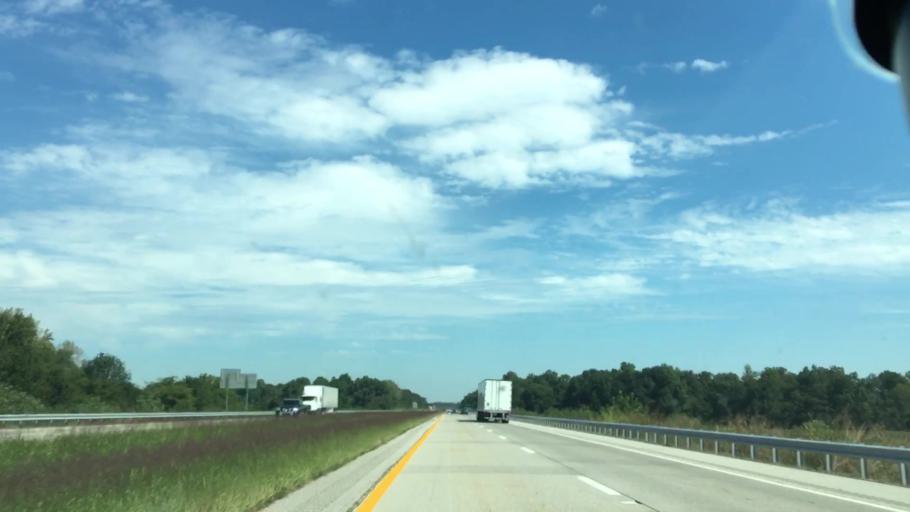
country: US
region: Kentucky
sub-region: Daviess County
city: Owensboro
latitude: 37.7592
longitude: -87.2470
